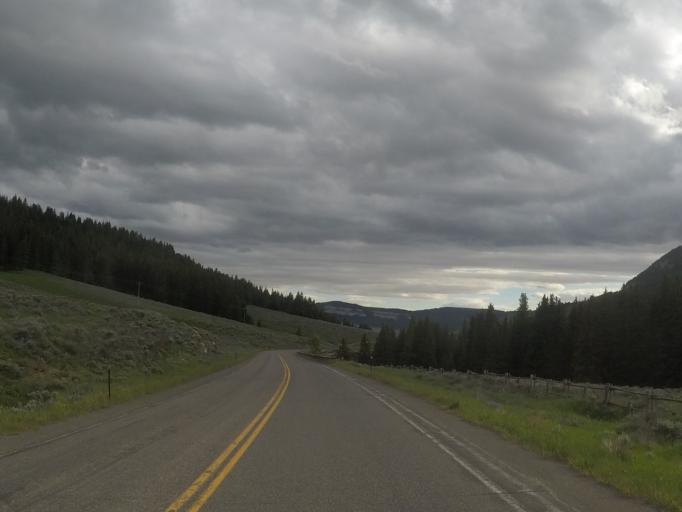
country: US
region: Wyoming
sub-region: Big Horn County
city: Greybull
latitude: 44.6074
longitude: -107.5276
